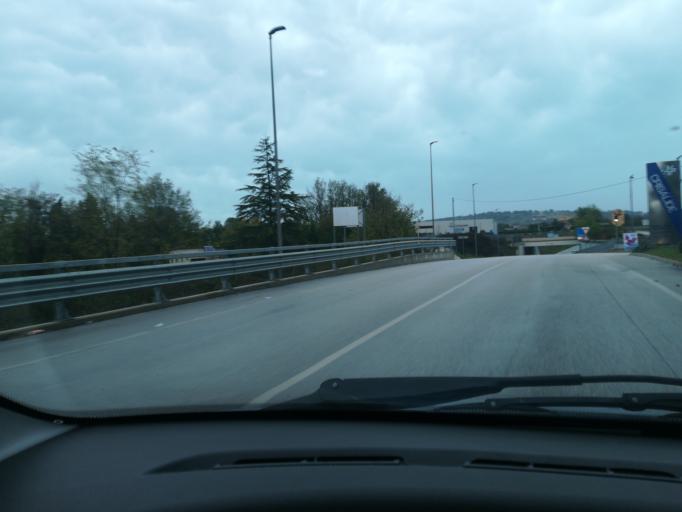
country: IT
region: The Marches
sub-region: Provincia di Macerata
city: Borgo Stazione
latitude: 43.2887
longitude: 13.6515
